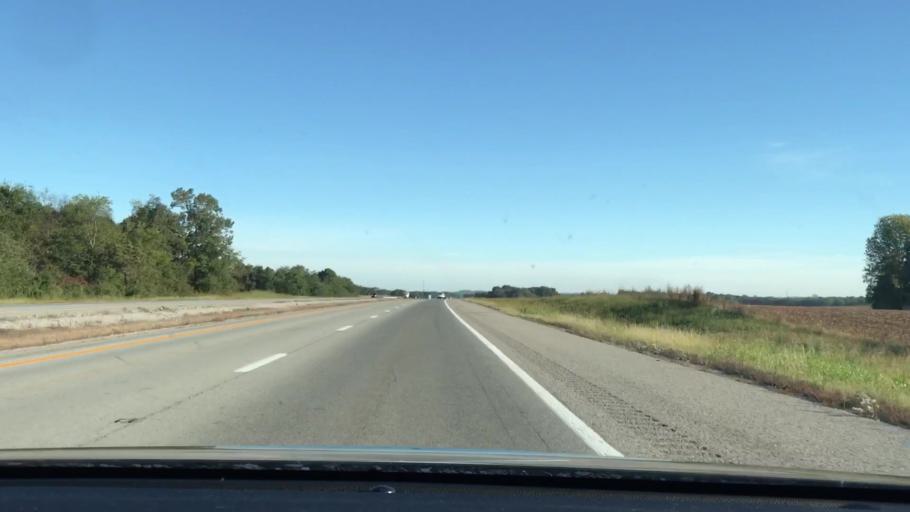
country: US
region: Kentucky
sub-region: Christian County
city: Hopkinsville
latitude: 36.7801
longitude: -87.4975
